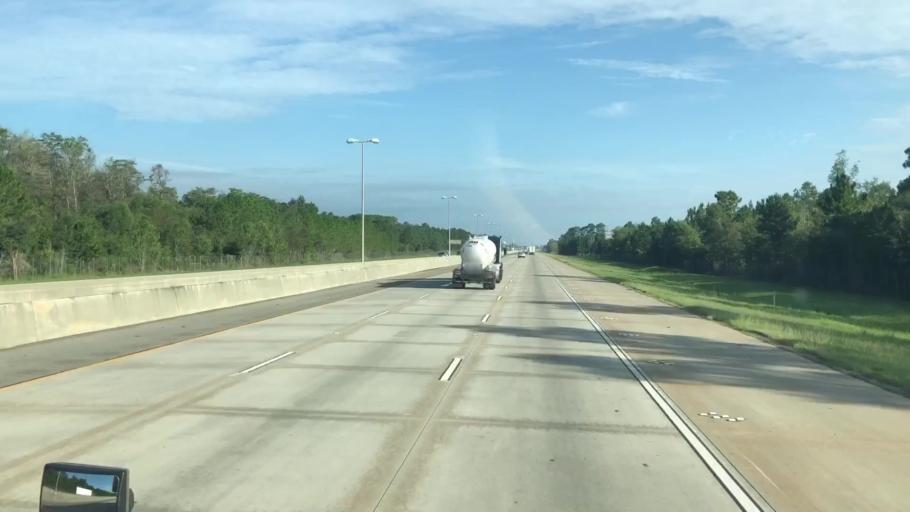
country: US
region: Georgia
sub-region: Cook County
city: Adel
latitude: 31.0843
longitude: -83.4127
